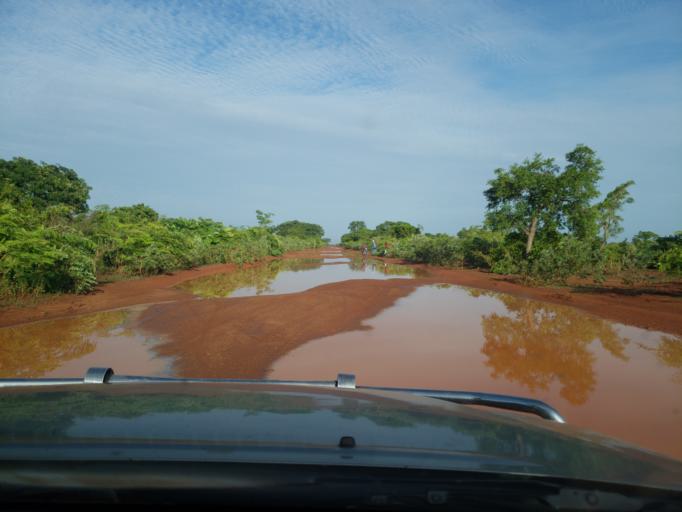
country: ML
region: Sikasso
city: Koutiala
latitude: 12.4271
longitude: -5.6353
